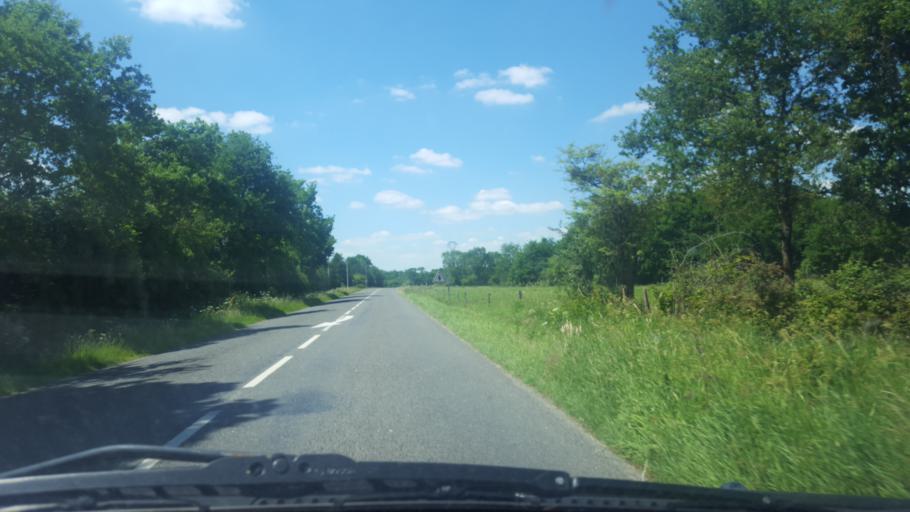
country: FR
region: Pays de la Loire
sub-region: Departement de la Vendee
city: Saint-Philbert-de-Bouaine
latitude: 46.9971
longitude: -1.5548
